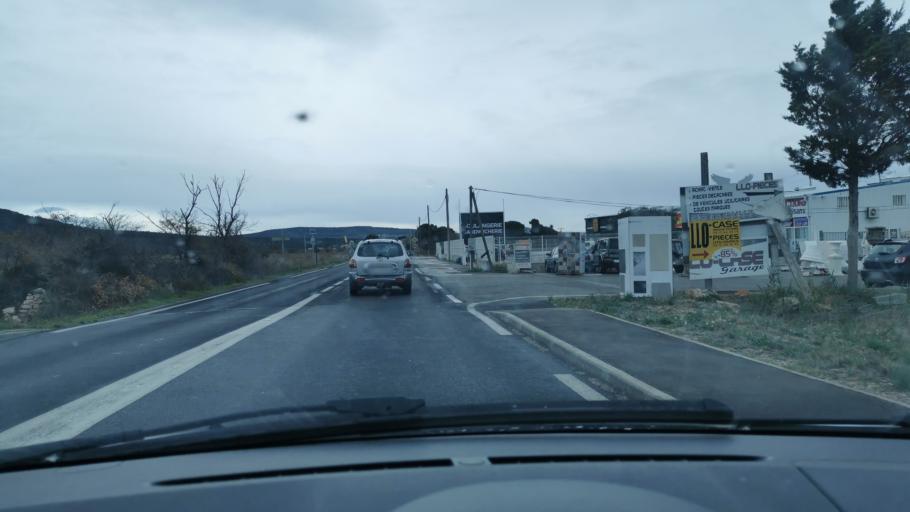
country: FR
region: Languedoc-Roussillon
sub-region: Departement de l'Herault
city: Frontignan
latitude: 43.4746
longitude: 3.7705
